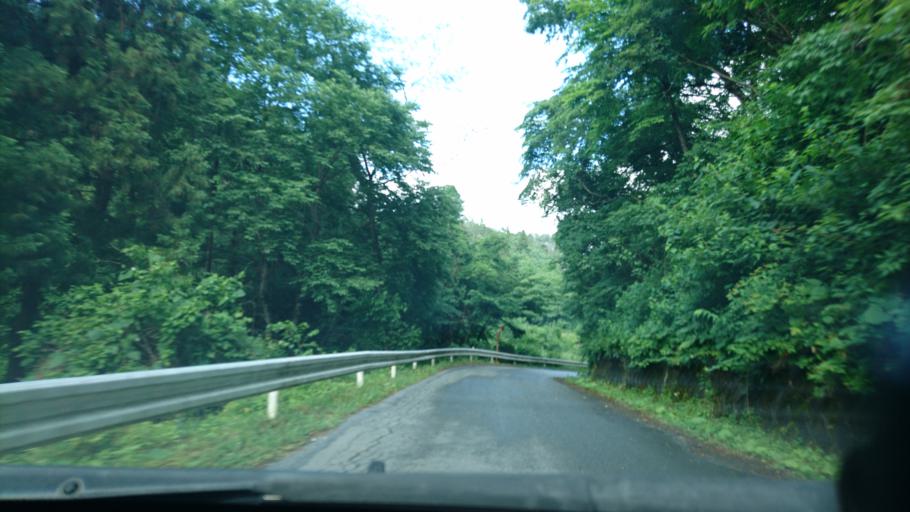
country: JP
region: Iwate
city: Ichinoseki
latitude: 38.8696
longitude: 141.2815
